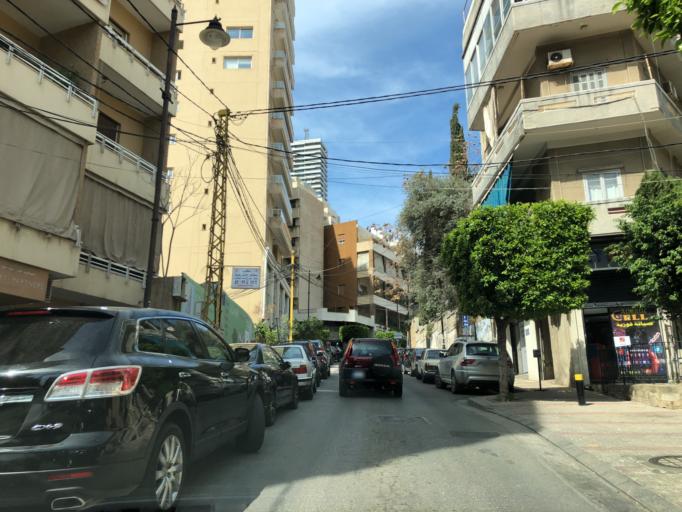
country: LB
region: Beyrouth
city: Beirut
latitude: 33.8841
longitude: 35.5190
